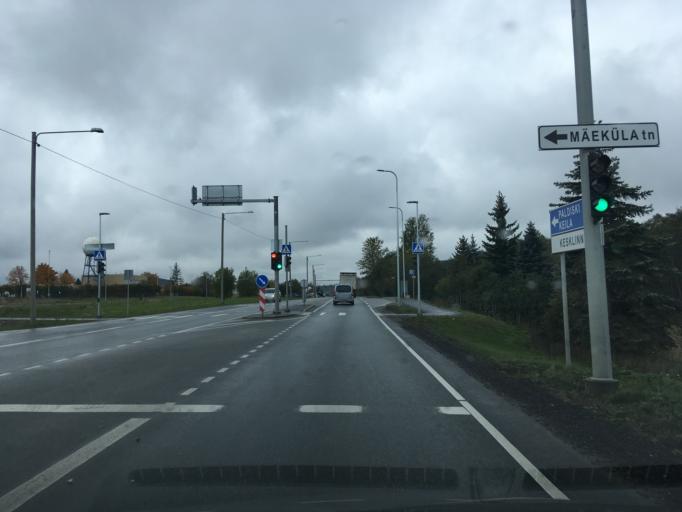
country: EE
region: Harju
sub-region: Saue vald
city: Laagri
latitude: 59.3992
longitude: 24.6038
